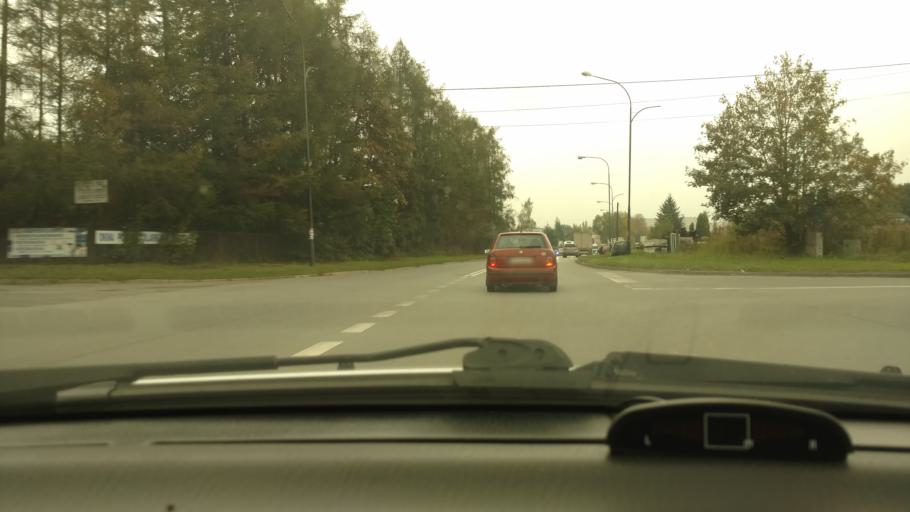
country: PL
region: Lesser Poland Voivodeship
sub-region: Powiat nowosadecki
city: Nowy Sacz
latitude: 49.6366
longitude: 20.7032
